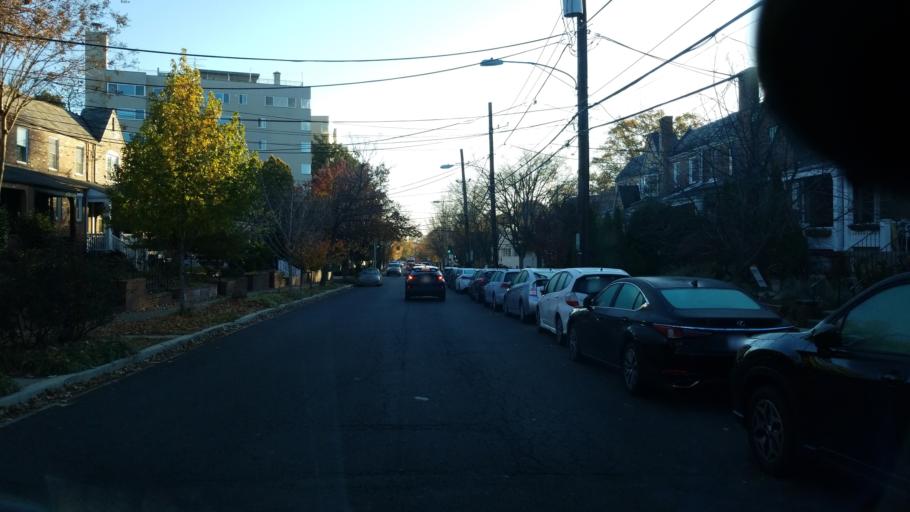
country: US
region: Maryland
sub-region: Montgomery County
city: Friendship Village
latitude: 38.9226
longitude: -77.0758
